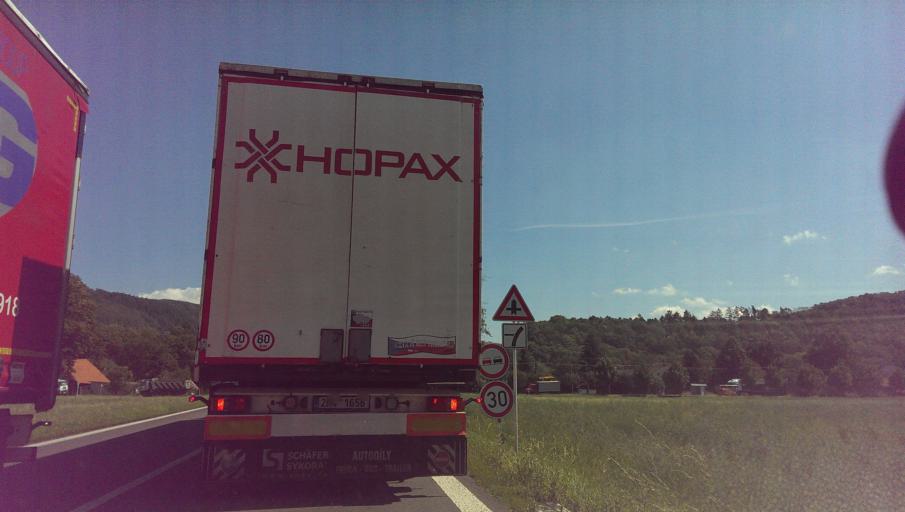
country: CZ
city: Lichnov (o. Novy Jicin)
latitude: 49.5980
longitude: 18.1873
